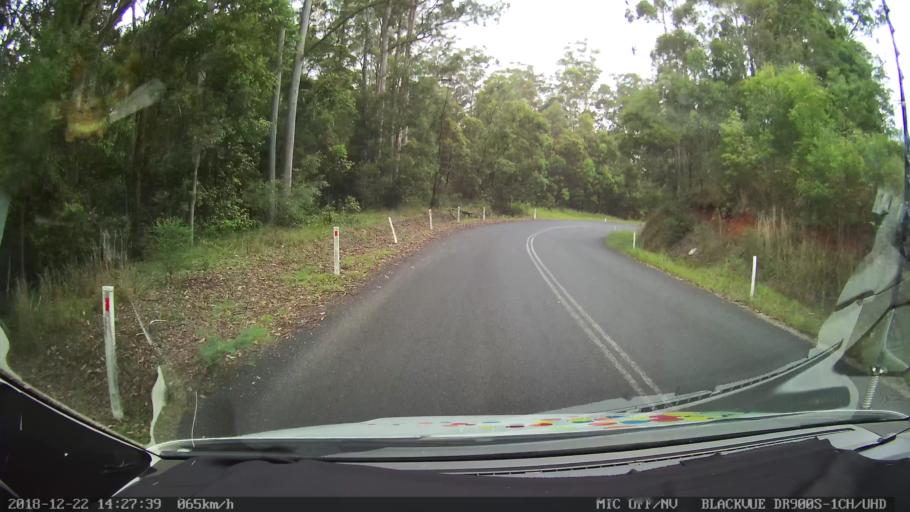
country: AU
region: New South Wales
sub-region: Bellingen
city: Dorrigo
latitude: -30.0672
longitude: 152.6360
